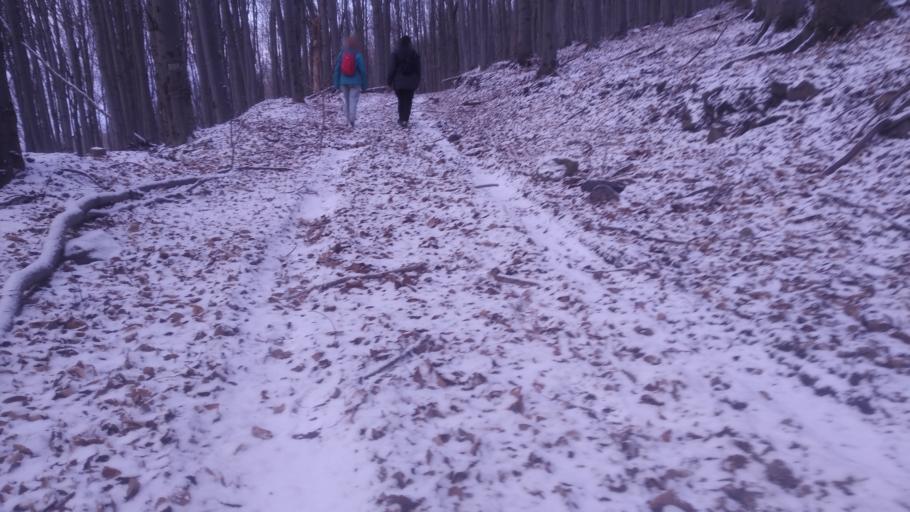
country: SK
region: Nitriansky
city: Sahy
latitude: 47.9663
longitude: 18.9263
